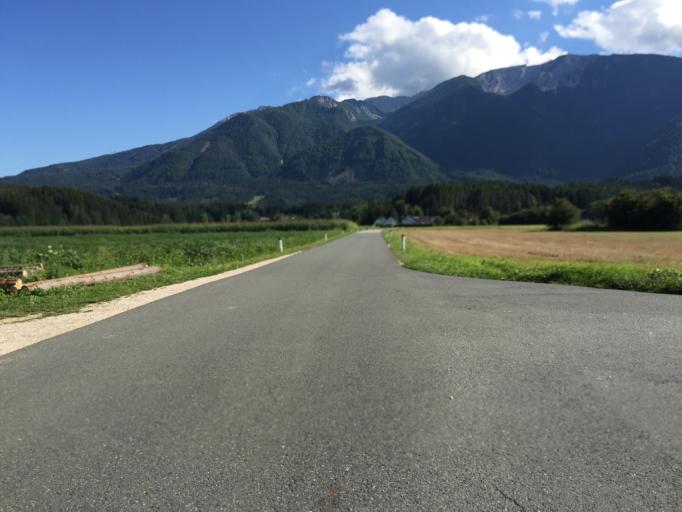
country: AT
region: Carinthia
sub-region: Politischer Bezirk Volkermarkt
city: Feistritz ob Bleiburg
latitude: 46.5619
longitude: 14.7673
